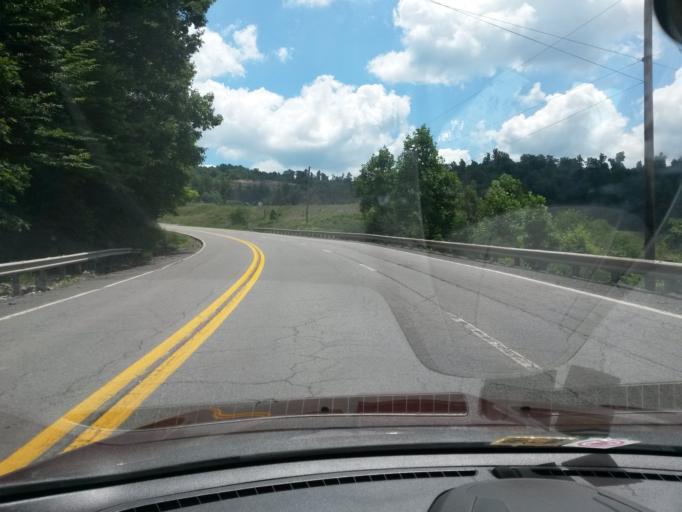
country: US
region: West Virginia
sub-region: Raleigh County
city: Sophia
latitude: 37.7193
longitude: -81.2601
